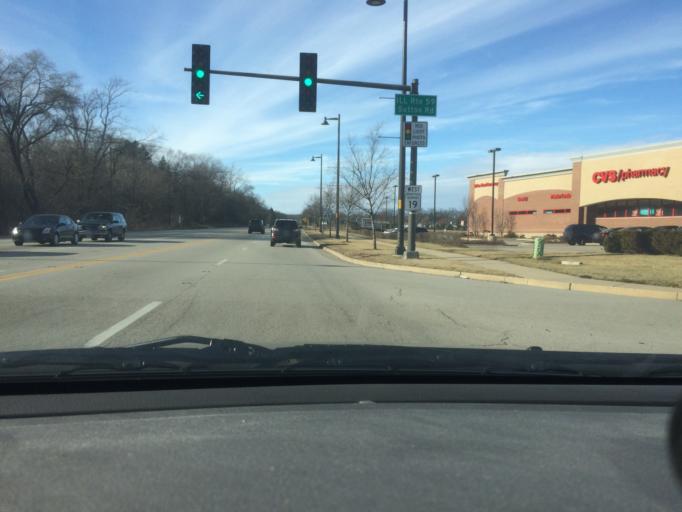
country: US
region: Illinois
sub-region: Cook County
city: Streamwood
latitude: 42.0193
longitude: -88.2032
